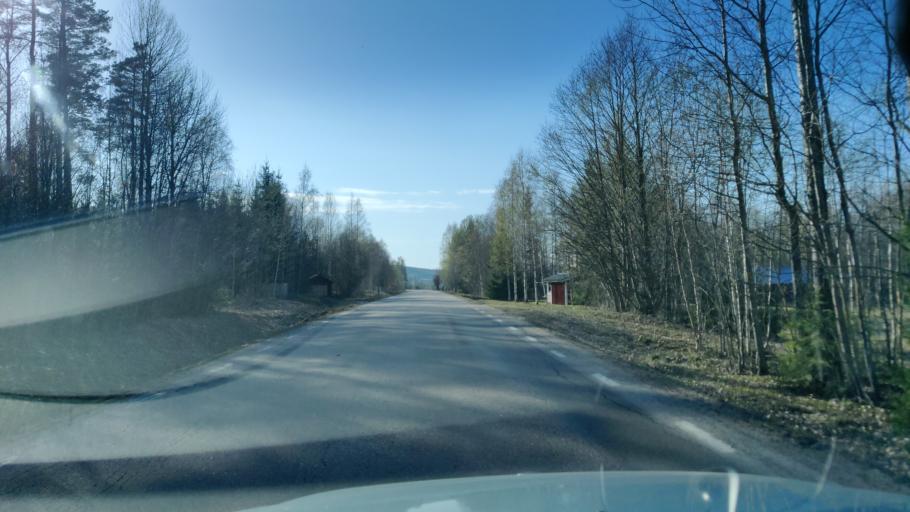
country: SE
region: Vaermland
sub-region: Munkfors Kommun
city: Munkfors
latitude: 59.9698
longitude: 13.4601
